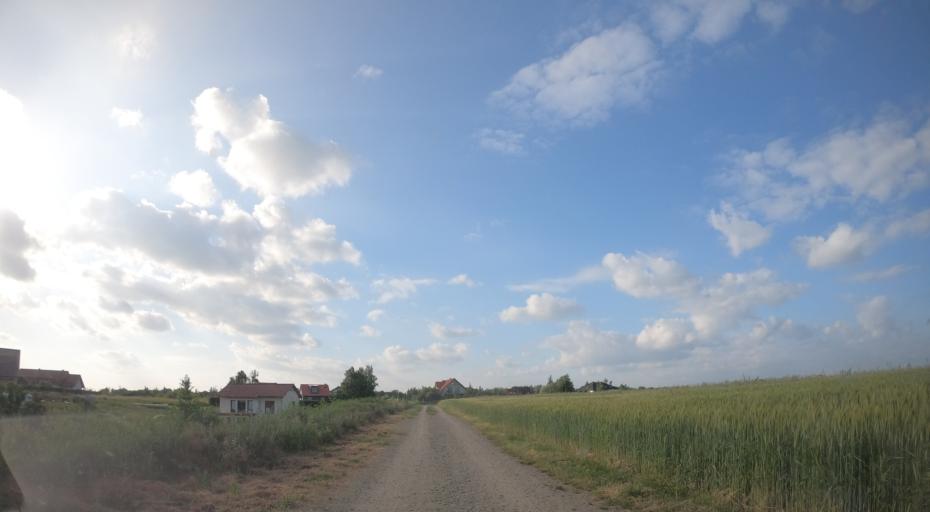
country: PL
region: Lubusz
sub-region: Powiat gorzowski
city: Santok
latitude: 52.7392
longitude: 15.3984
